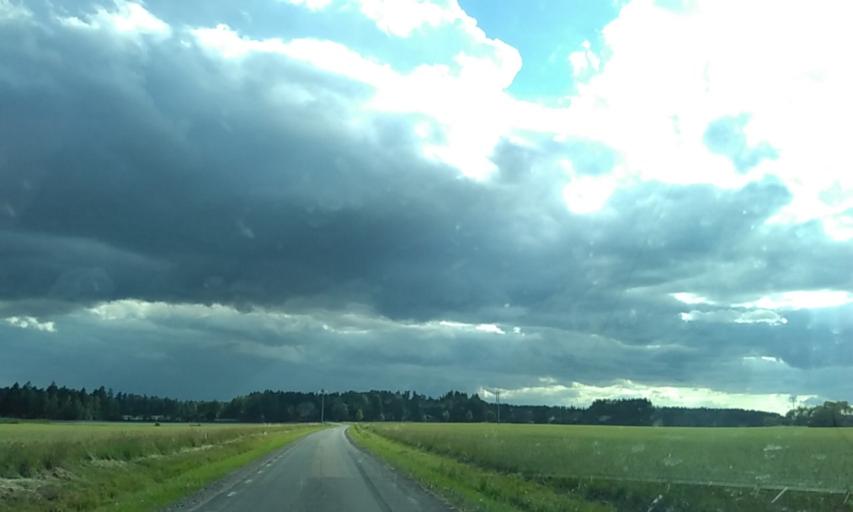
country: SE
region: Vaestra Goetaland
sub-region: Lidkopings Kommun
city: Lidkoping
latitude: 58.5616
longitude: 13.0178
